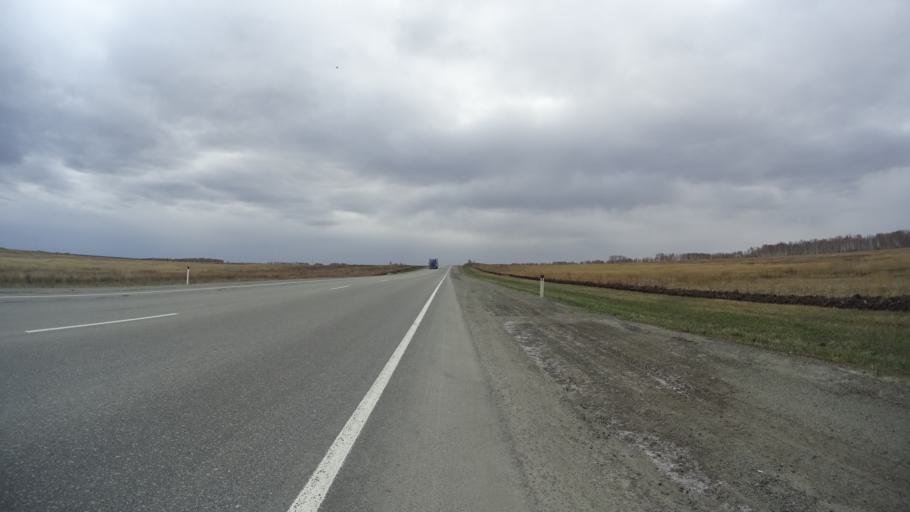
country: RU
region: Chelyabinsk
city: Yemanzhelinsk
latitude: 54.7096
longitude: 61.2592
